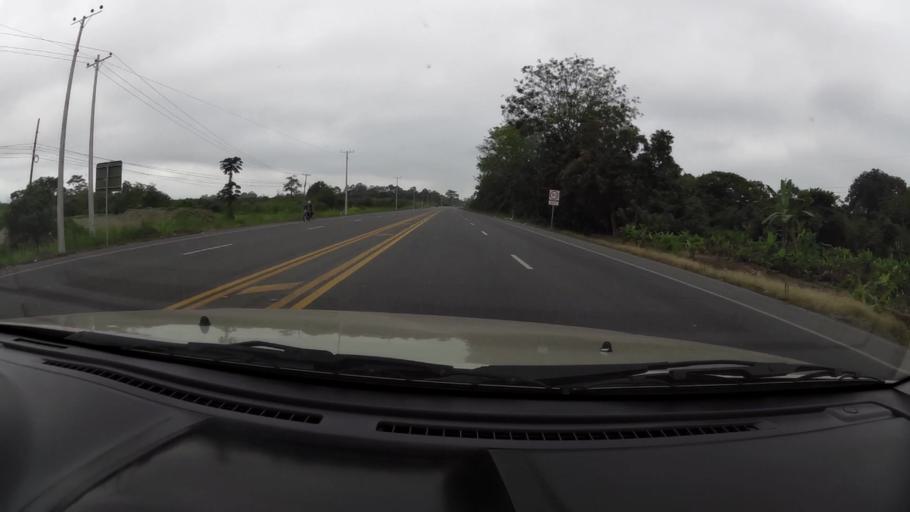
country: EC
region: Guayas
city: Naranjal
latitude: -2.5589
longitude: -79.5569
